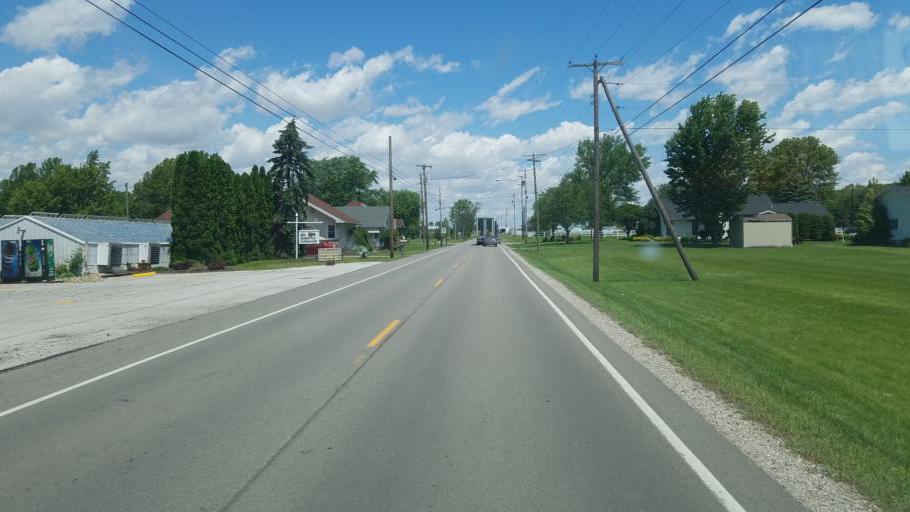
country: US
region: Ohio
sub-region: Huron County
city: Willard
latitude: 41.0311
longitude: -82.7318
